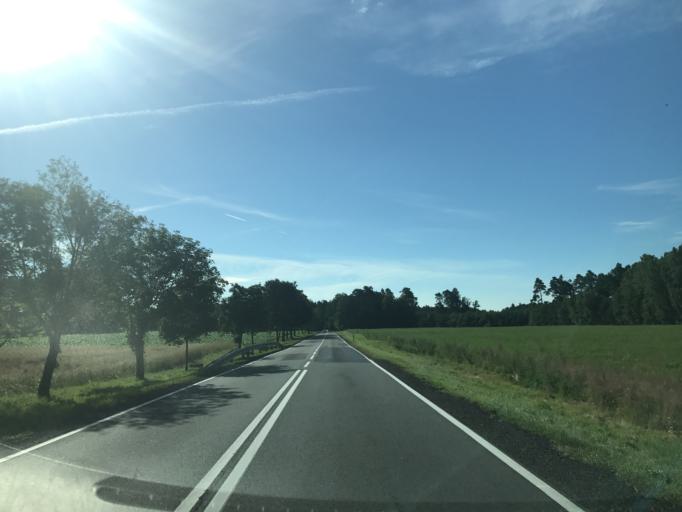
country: PL
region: Pomeranian Voivodeship
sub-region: Powiat czluchowski
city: Przechlewo
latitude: 53.7061
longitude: 17.2651
